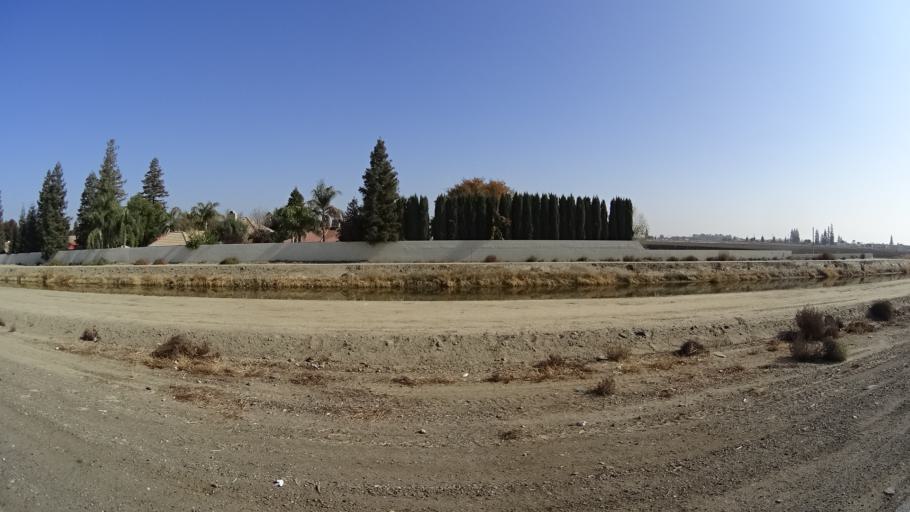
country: US
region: California
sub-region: Kern County
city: Greenfield
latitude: 35.2708
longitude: -119.0213
